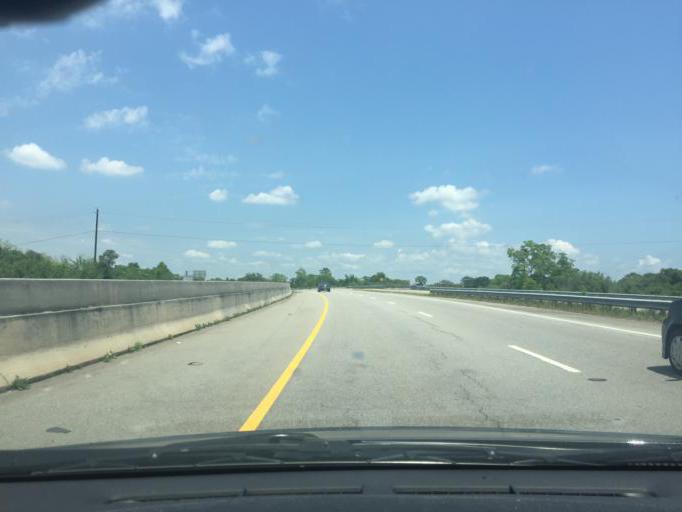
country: US
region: Georgia
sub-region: Chatham County
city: Thunderbolt
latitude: 32.0591
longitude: -81.0718
